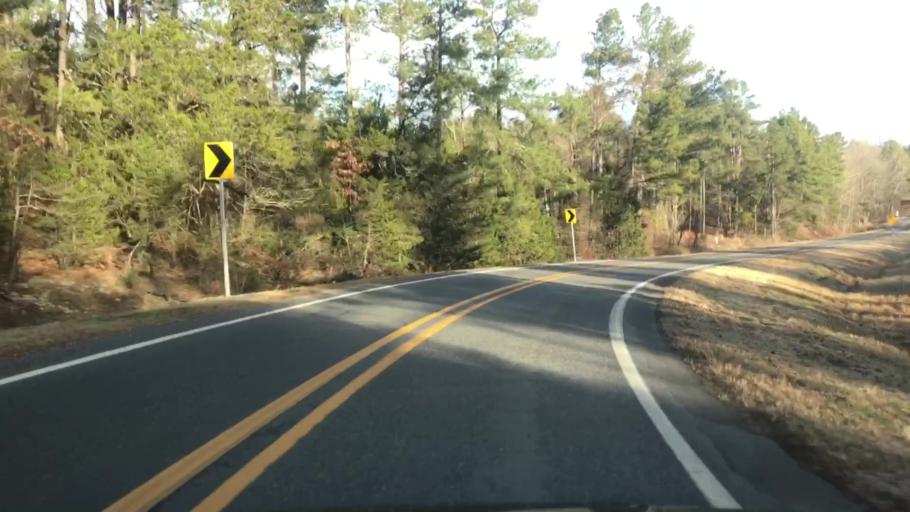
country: US
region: Arkansas
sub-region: Garland County
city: Rockwell
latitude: 34.4890
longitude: -93.2761
